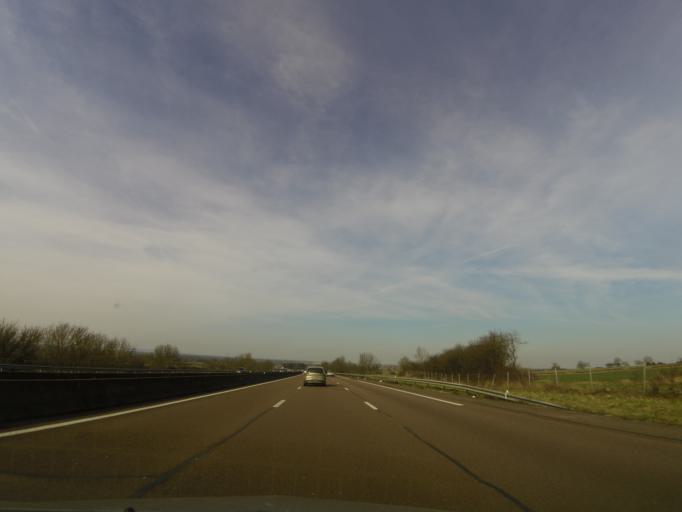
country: FR
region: Bourgogne
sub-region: Departement de Saone-et-Loire
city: Sennecey-le-Grand
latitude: 46.6516
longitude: 4.8589
